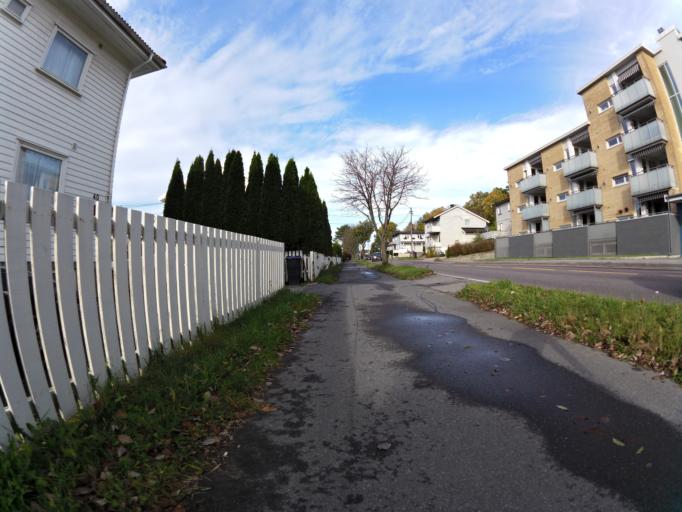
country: NO
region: Ostfold
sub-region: Fredrikstad
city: Fredrikstad
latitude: 59.2254
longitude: 10.9292
